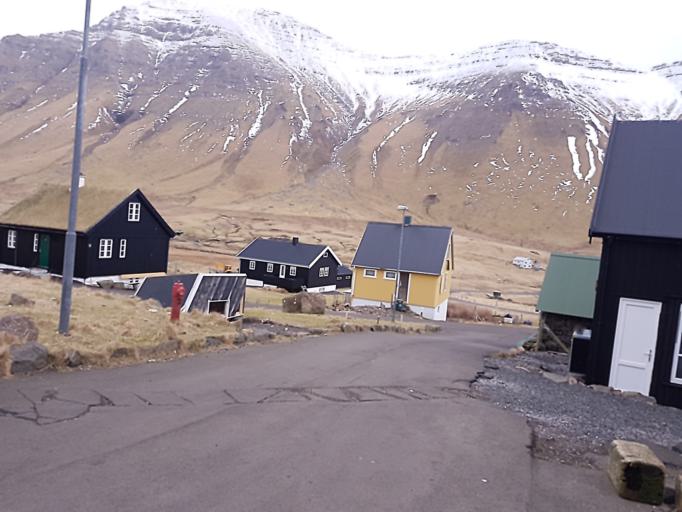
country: FO
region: Vagar
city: Sorvagur
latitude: 62.1105
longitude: -7.4390
